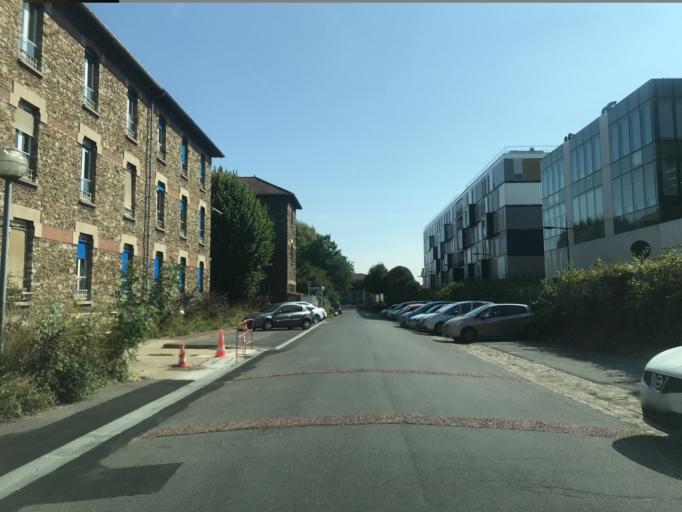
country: FR
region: Ile-de-France
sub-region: Departement du Val-de-Marne
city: Villejuif
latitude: 48.7959
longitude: 2.3602
